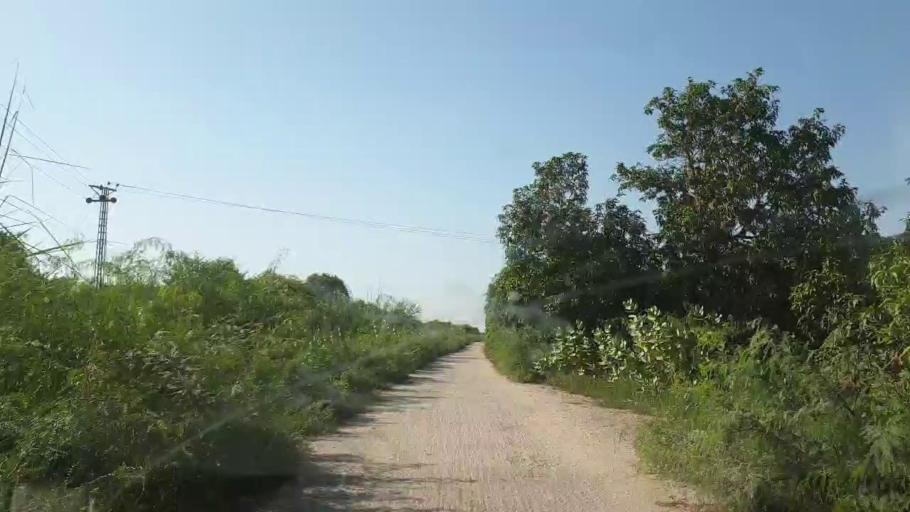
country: PK
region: Sindh
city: Tando Jam
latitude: 25.3296
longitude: 68.5910
